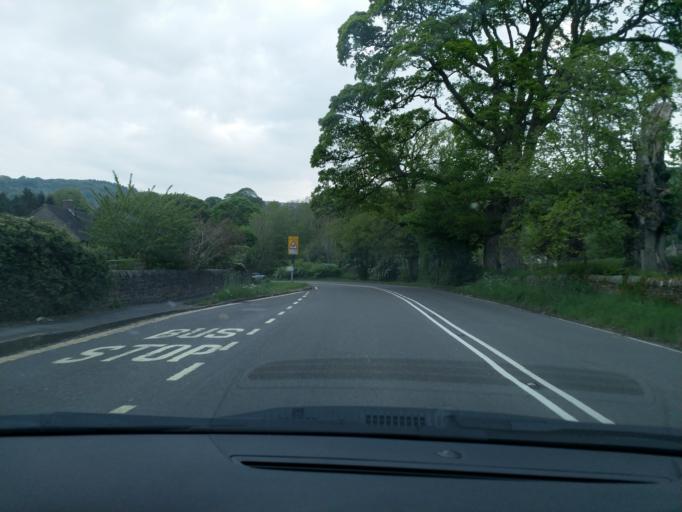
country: GB
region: England
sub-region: Derbyshire
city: Hathersage
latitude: 53.3298
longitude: -1.6503
